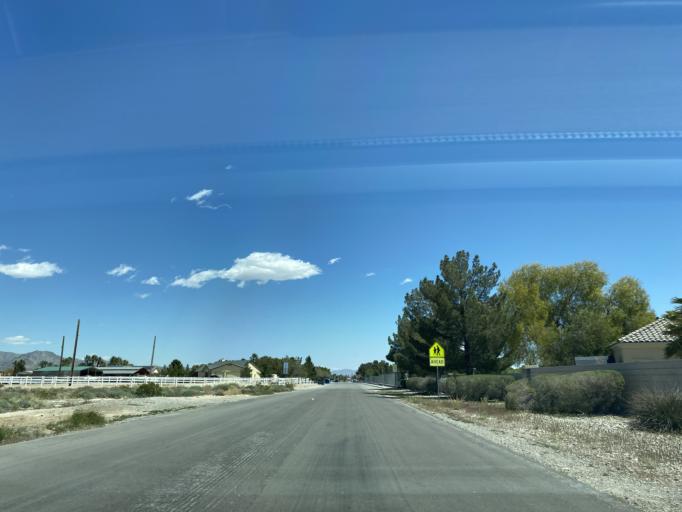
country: US
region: Nevada
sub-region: Clark County
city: North Las Vegas
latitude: 36.3090
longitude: -115.2364
